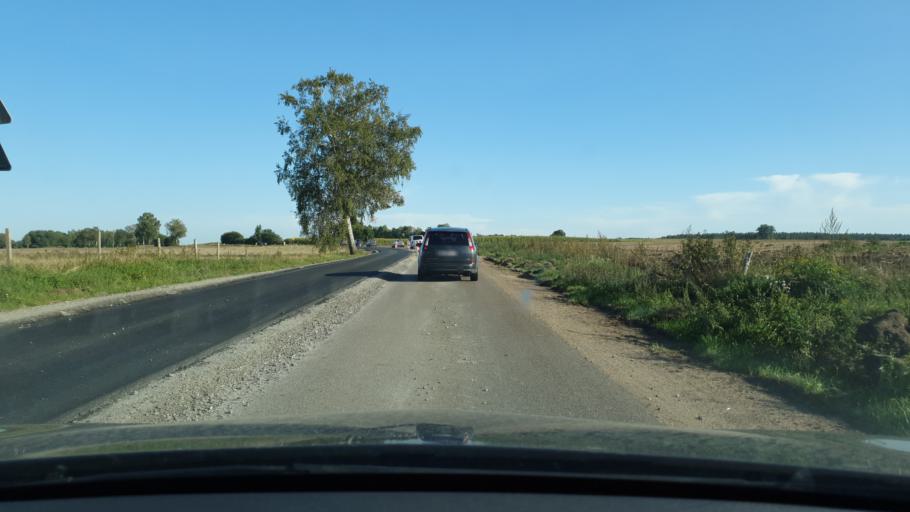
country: PL
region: West Pomeranian Voivodeship
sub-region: Powiat gryficki
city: Ploty
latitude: 53.8143
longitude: 15.1720
